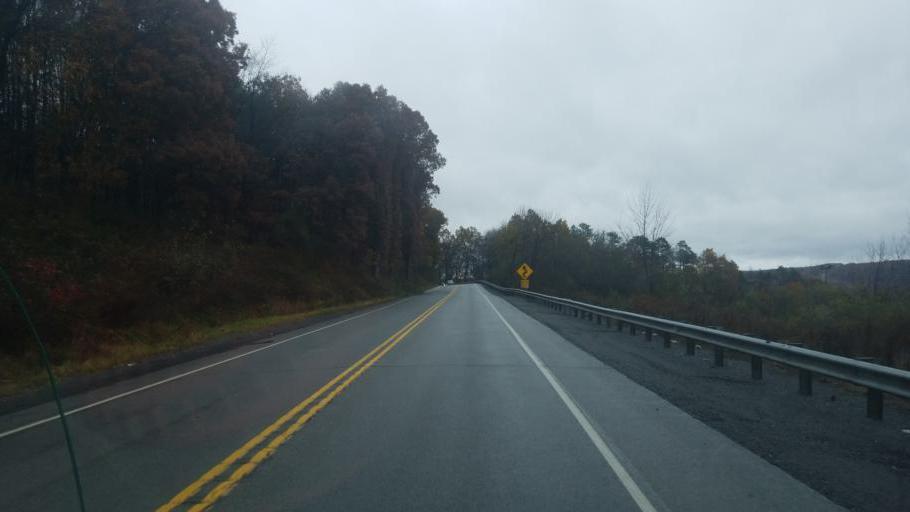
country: US
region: Pennsylvania
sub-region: Clearfield County
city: Clearfield
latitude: 41.0428
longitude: -78.3924
